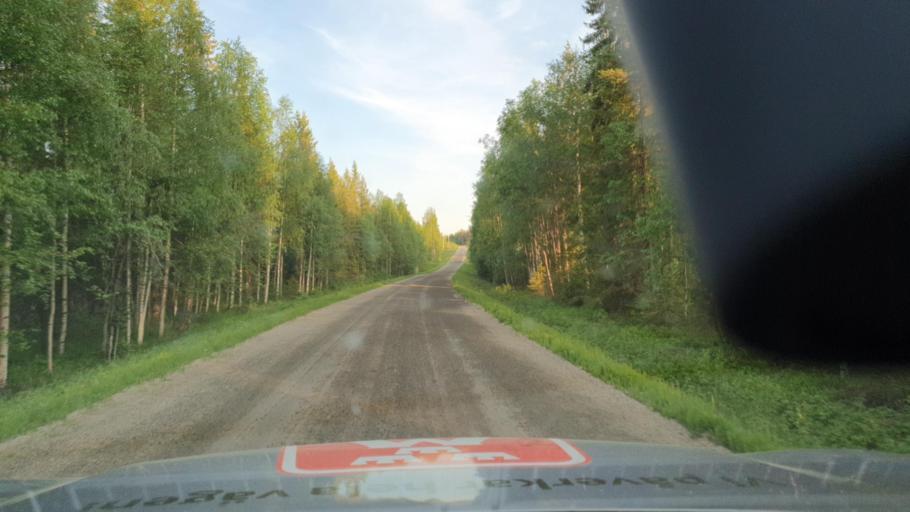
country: SE
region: Norrbotten
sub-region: Bodens Kommun
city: Boden
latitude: 66.1906
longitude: 21.5014
